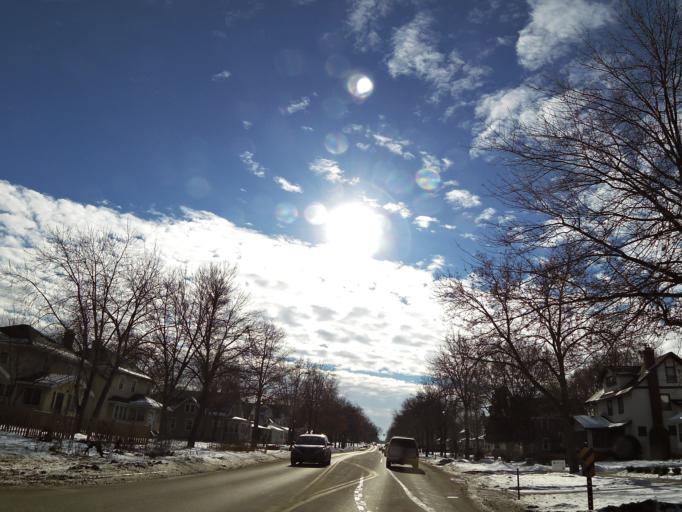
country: US
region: Minnesota
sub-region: Hennepin County
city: Richfield
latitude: 44.9329
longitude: -93.2883
